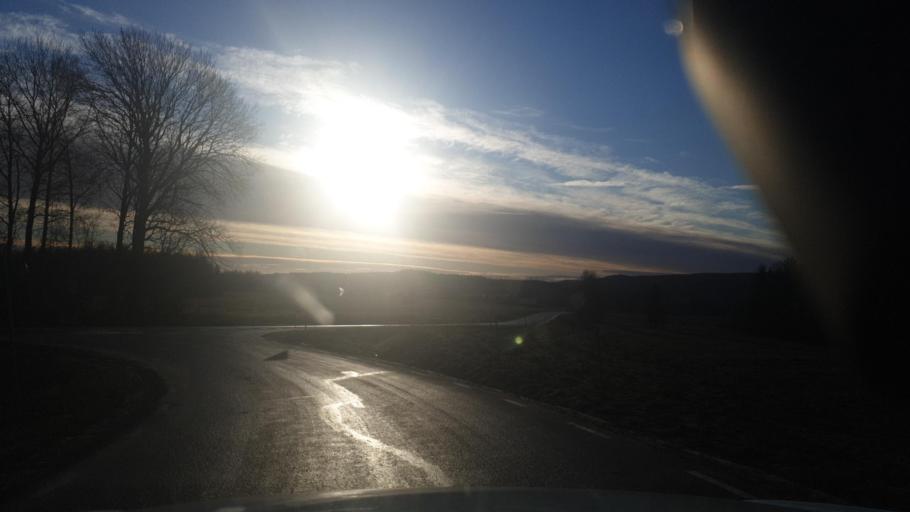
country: SE
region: Vaermland
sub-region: Sunne Kommun
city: Sunne
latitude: 59.7357
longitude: 13.1291
